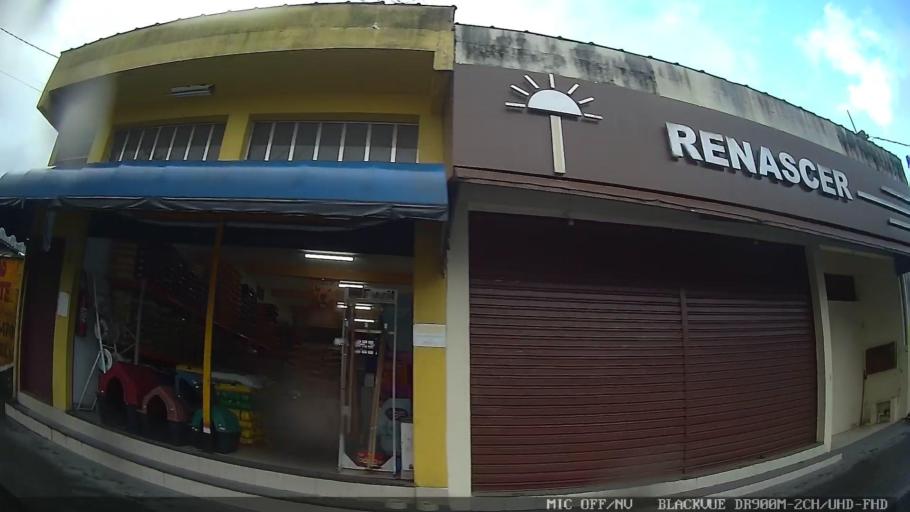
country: BR
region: Sao Paulo
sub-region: Itanhaem
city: Itanhaem
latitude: -24.1686
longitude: -46.7845
